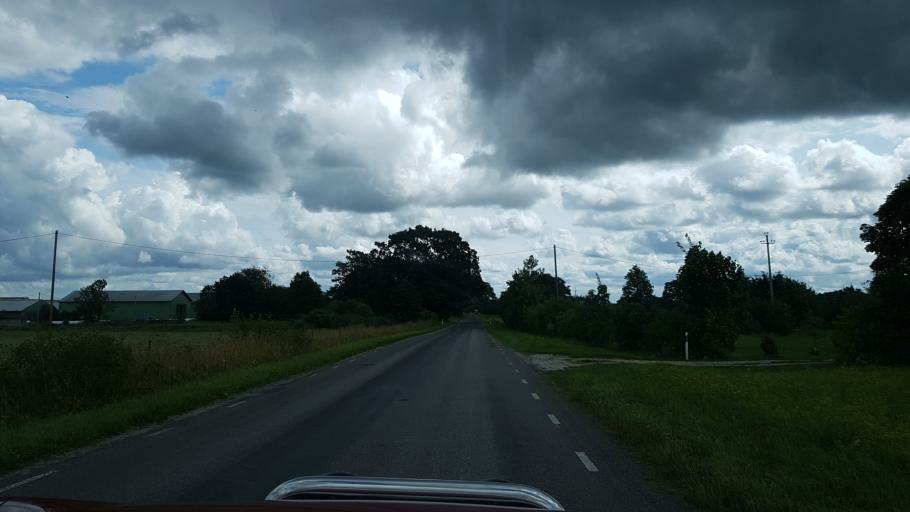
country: EE
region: Laeaene
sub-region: Lihula vald
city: Lihula
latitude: 58.7126
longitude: 24.0055
